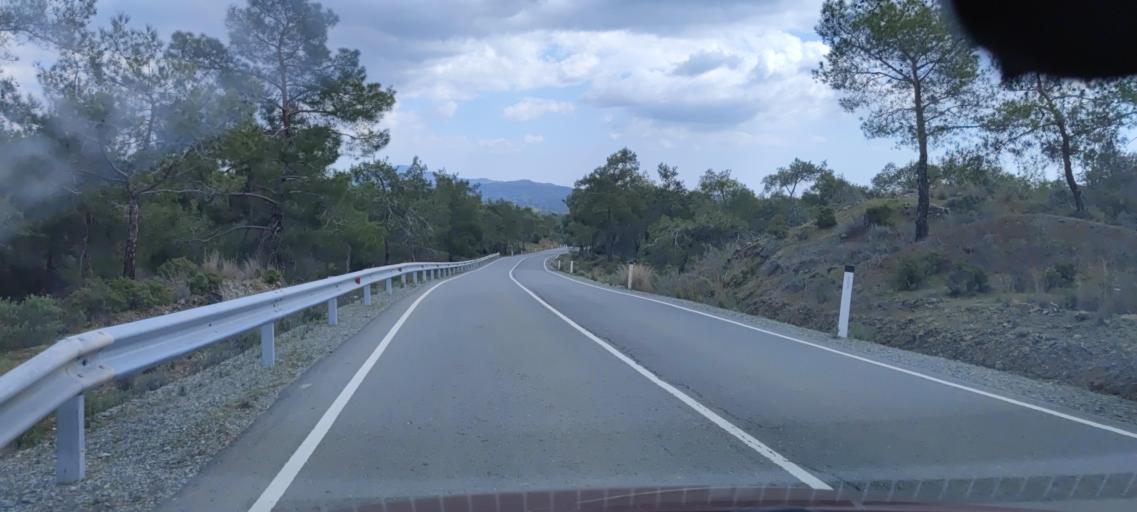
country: CY
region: Lefkosia
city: Lythrodontas
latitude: 34.9318
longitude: 33.3336
